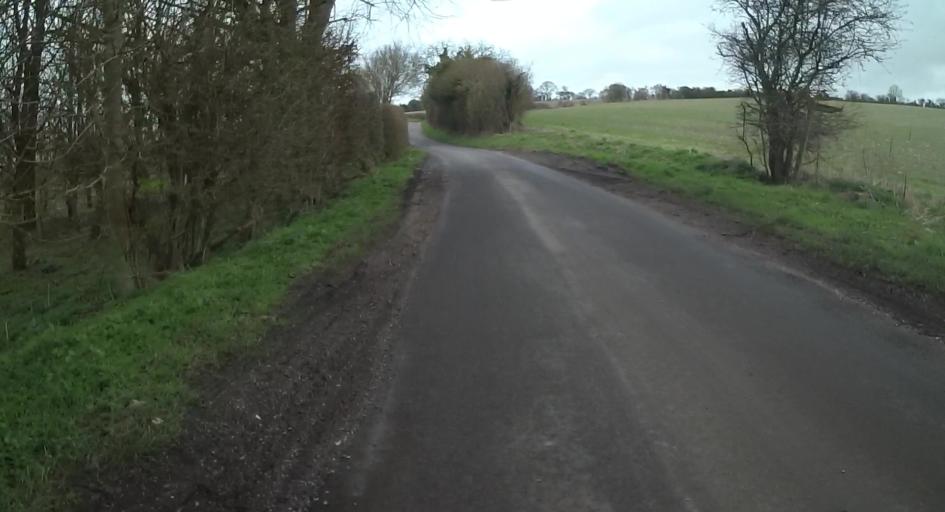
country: GB
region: England
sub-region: Hampshire
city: Kingsclere
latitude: 51.2860
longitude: -1.2254
